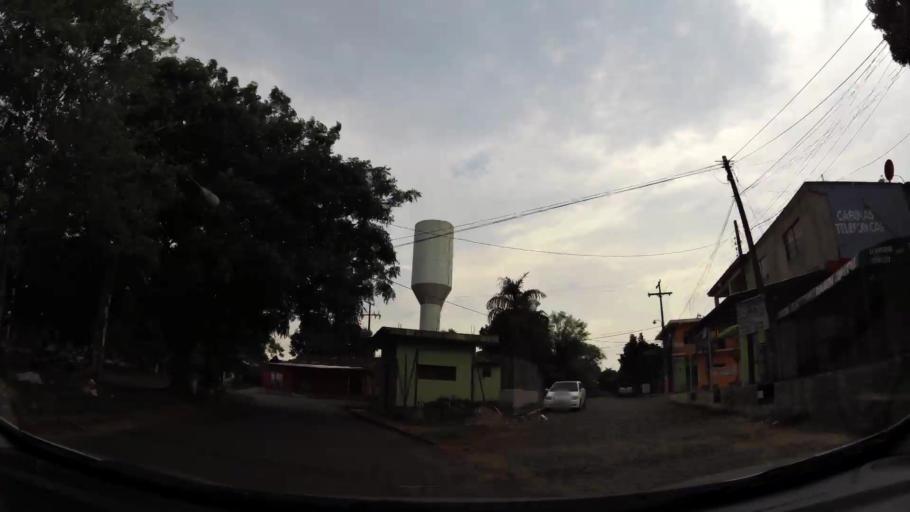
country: PY
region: Alto Parana
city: Presidente Franco
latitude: -25.5392
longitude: -54.6043
